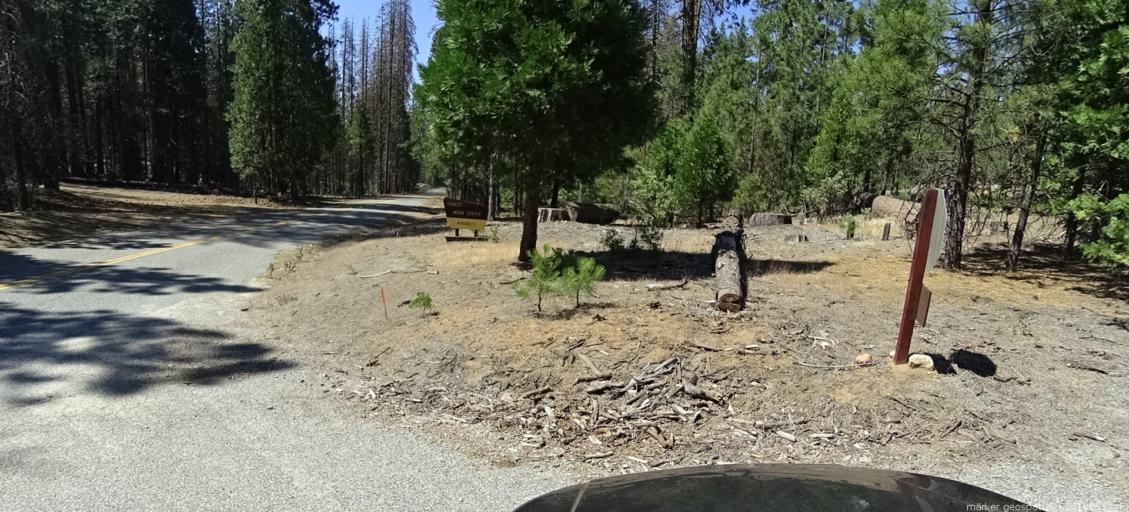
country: US
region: California
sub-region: Madera County
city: Oakhurst
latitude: 37.4089
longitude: -119.3480
